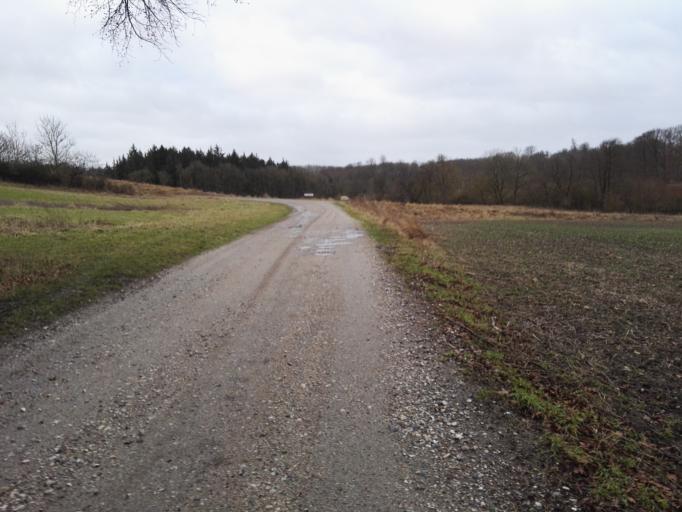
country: DK
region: Zealand
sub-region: Lejre Kommune
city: Lejre
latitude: 55.6403
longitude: 11.9300
